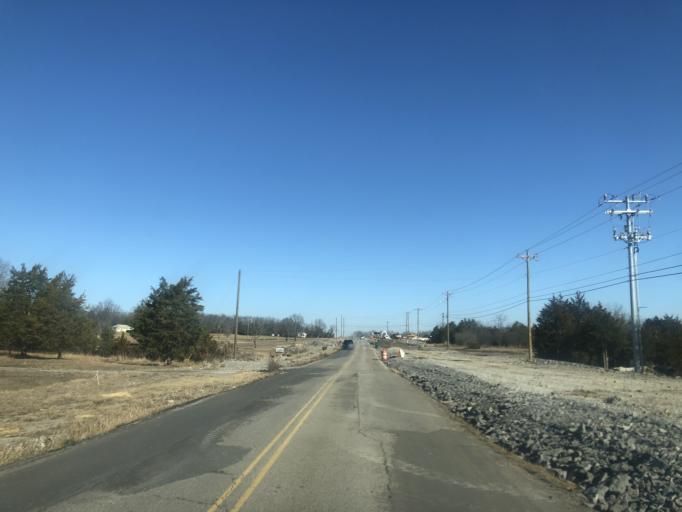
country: US
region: Tennessee
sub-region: Rutherford County
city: Smyrna
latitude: 35.9578
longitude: -86.5441
